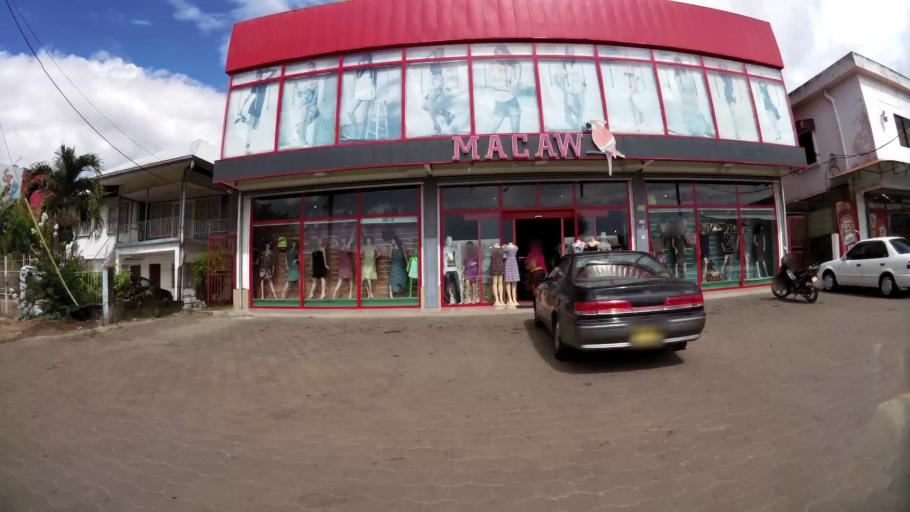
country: SR
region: Paramaribo
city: Paramaribo
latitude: 5.8420
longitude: -55.1440
